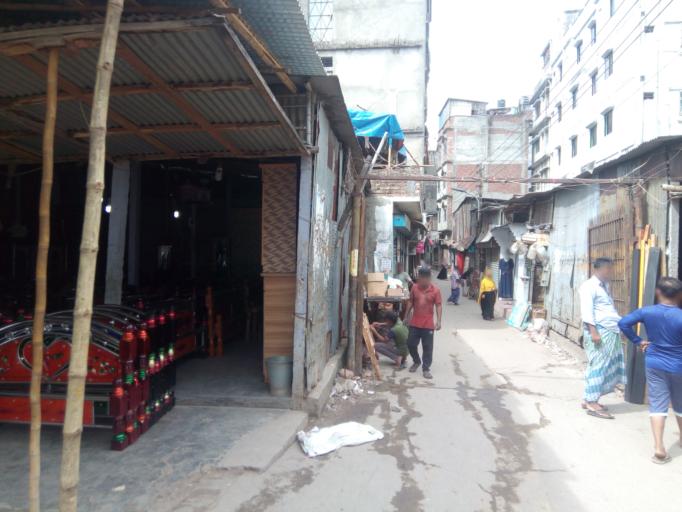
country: BD
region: Dhaka
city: Azimpur
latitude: 23.7222
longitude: 90.3753
